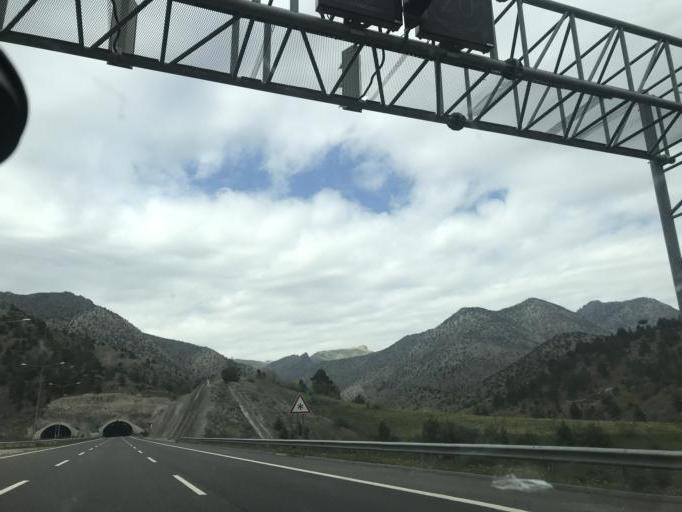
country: TR
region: Nigde
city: Ciftehan
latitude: 37.5186
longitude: 34.8177
